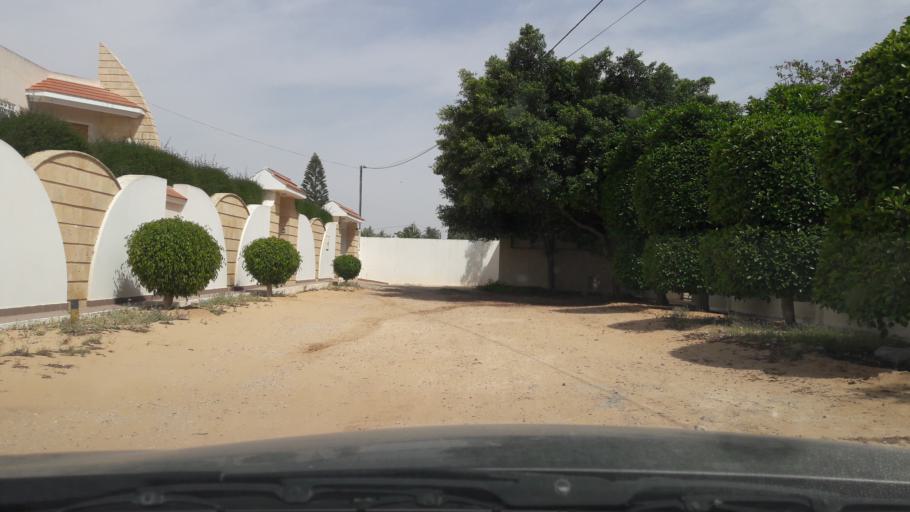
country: TN
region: Safaqis
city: Al Qarmadah
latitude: 34.7862
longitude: 10.7590
